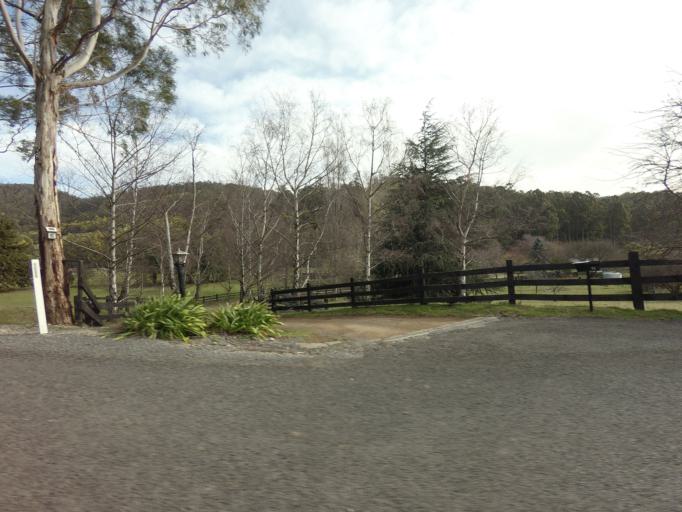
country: AU
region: Tasmania
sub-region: Kingborough
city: Margate
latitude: -42.9905
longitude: 147.1881
